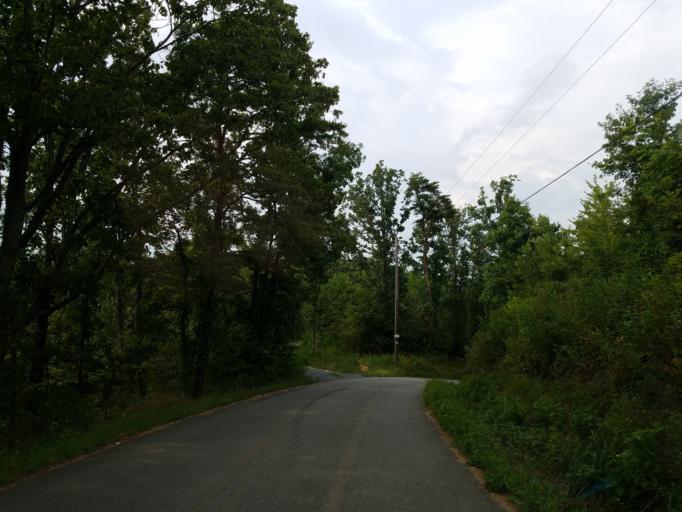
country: US
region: Georgia
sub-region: Bartow County
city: Rydal
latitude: 34.3737
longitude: -84.6852
